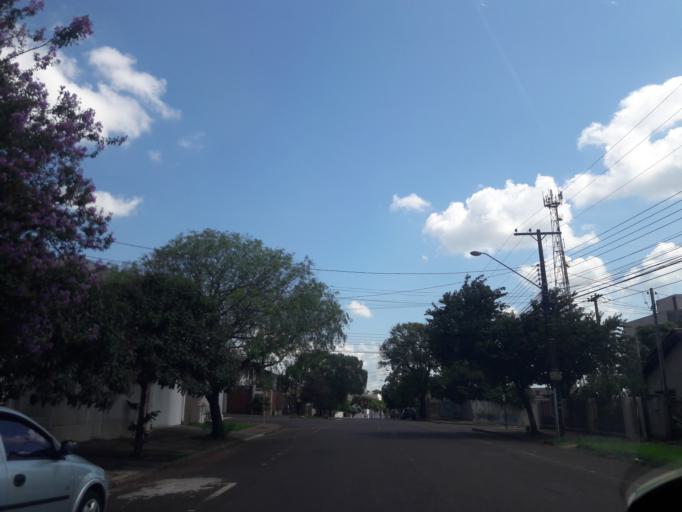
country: BR
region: Parana
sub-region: Cascavel
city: Cascavel
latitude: -24.9709
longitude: -53.4588
